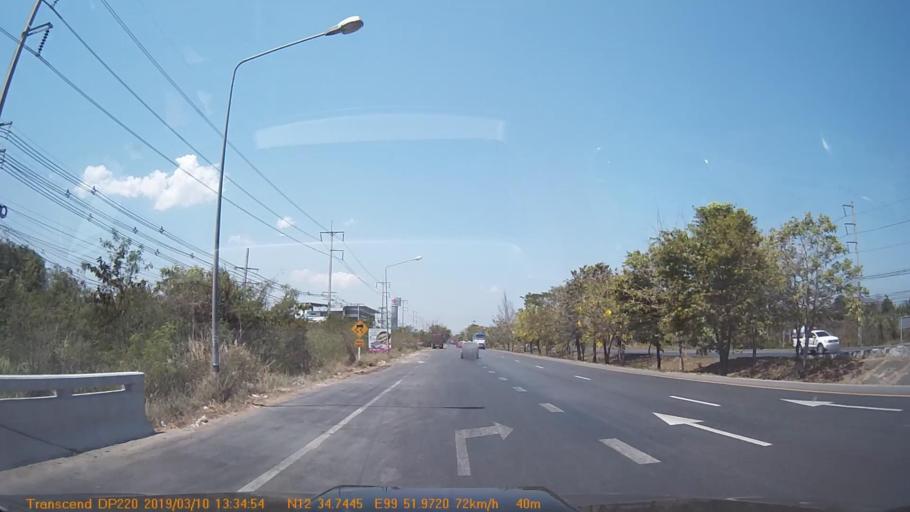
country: TH
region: Prachuap Khiri Khan
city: Hua Hin
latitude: 12.5793
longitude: 99.8662
